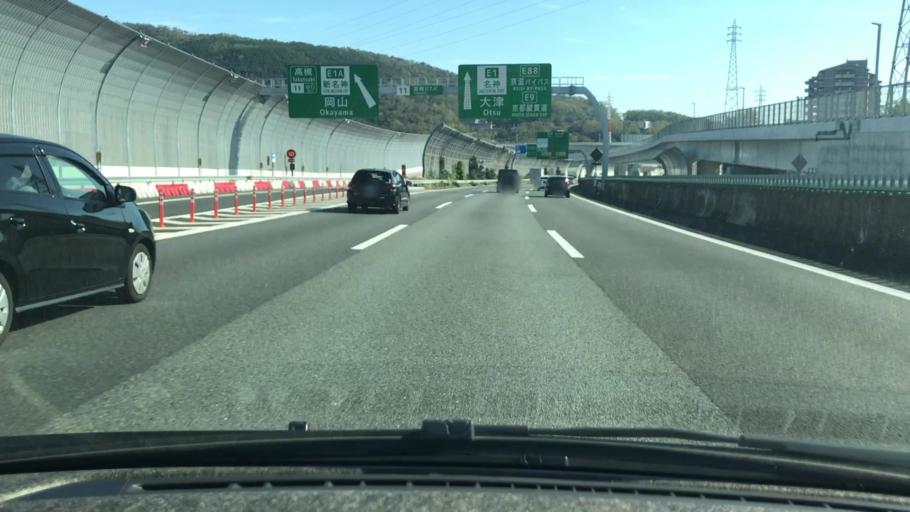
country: JP
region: Osaka
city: Takatsuki
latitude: 34.8678
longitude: 135.6220
